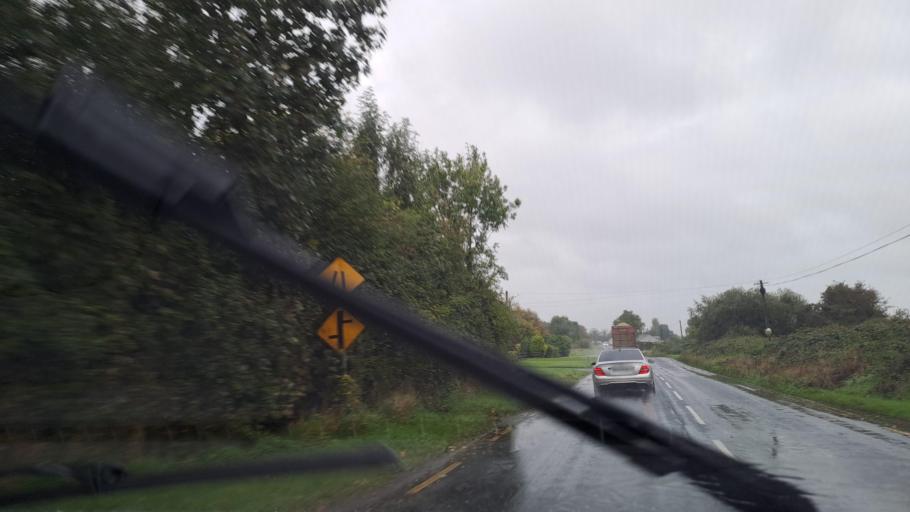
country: IE
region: Ulster
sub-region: County Monaghan
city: Carrickmacross
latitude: 53.9737
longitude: -6.6704
